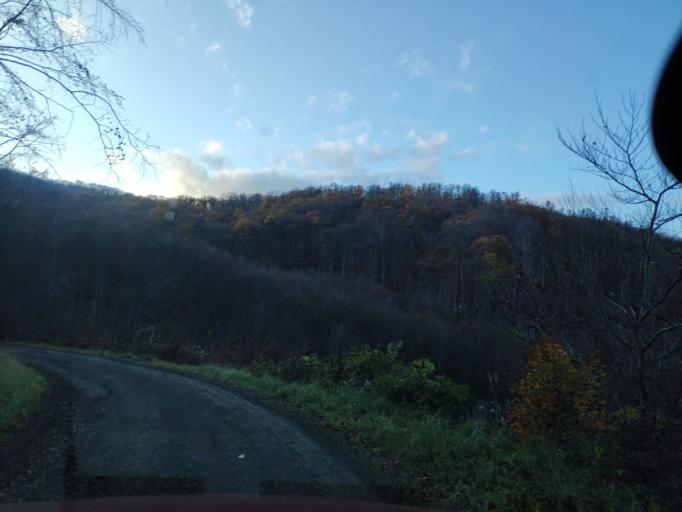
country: SK
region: Kosicky
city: Secovce
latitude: 48.5961
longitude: 21.5103
